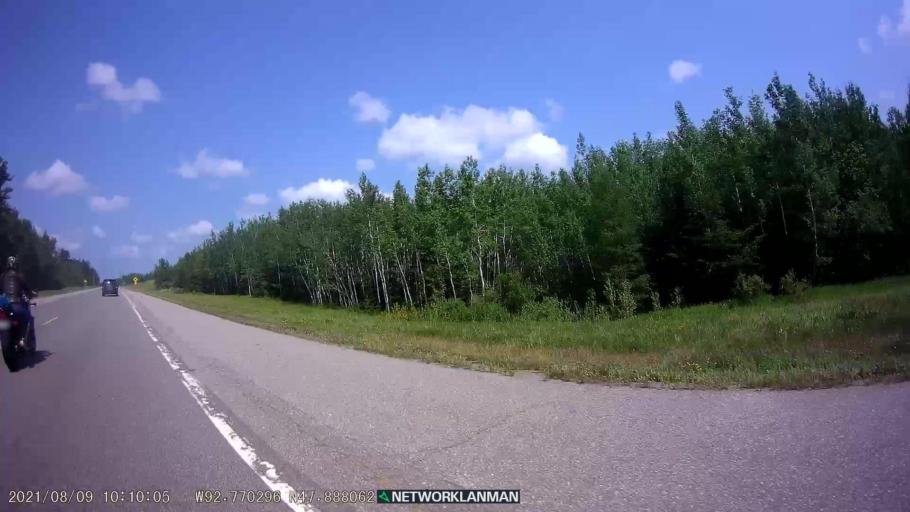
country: US
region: Minnesota
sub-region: Saint Louis County
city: Mountain Iron
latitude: 47.8873
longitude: -92.7689
